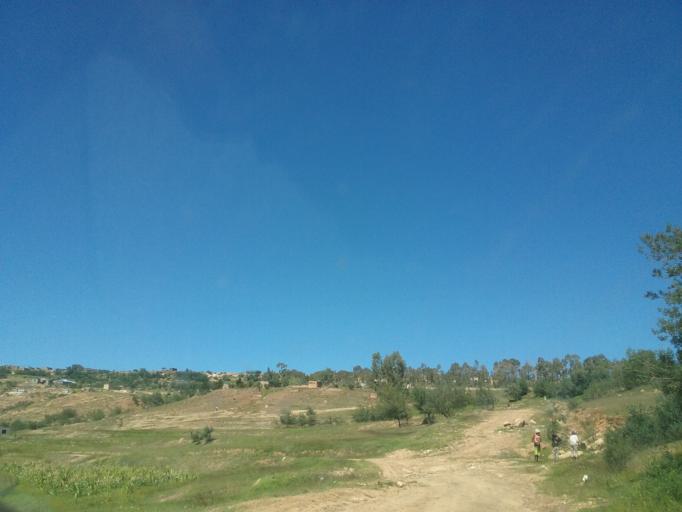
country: LS
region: Maseru
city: Maseru
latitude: -29.4032
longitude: 27.5750
